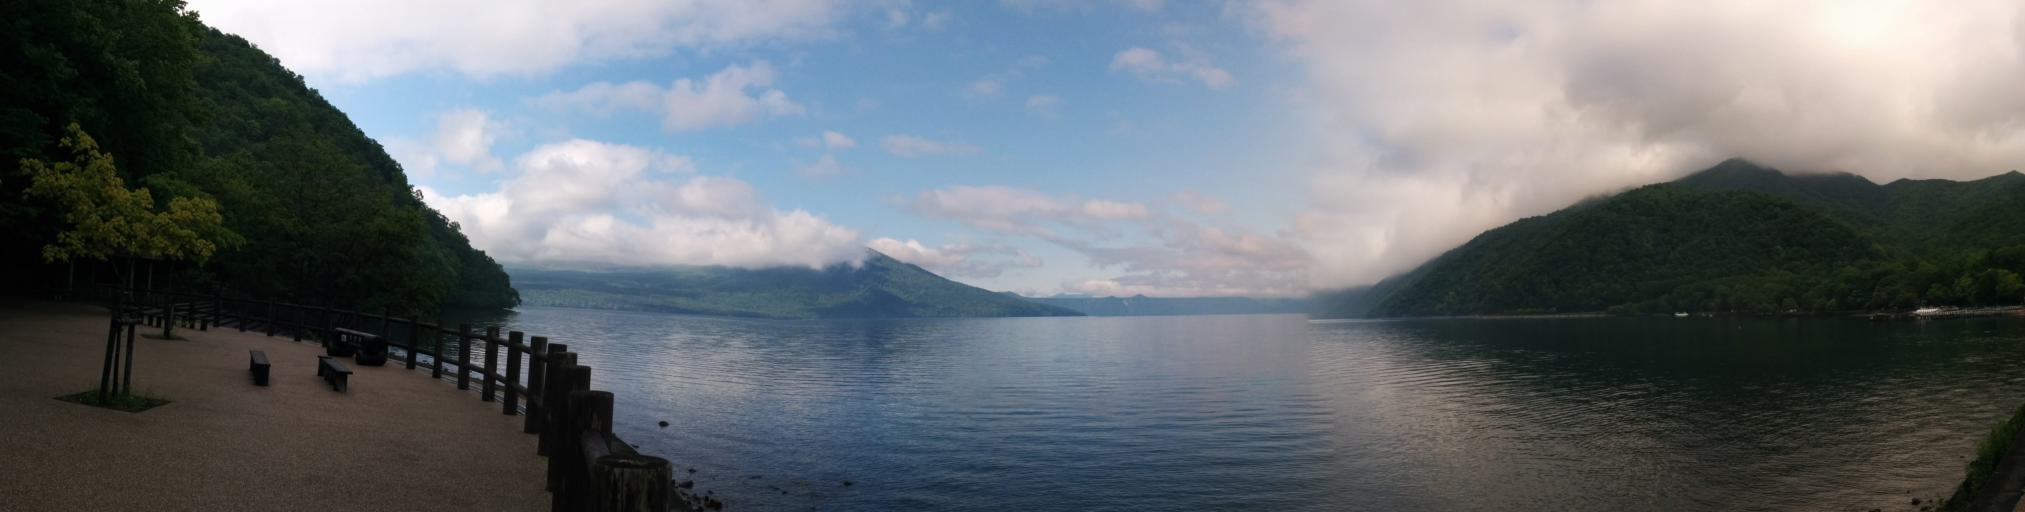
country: JP
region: Hokkaido
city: Shiraoi
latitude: 42.7697
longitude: 141.4026
